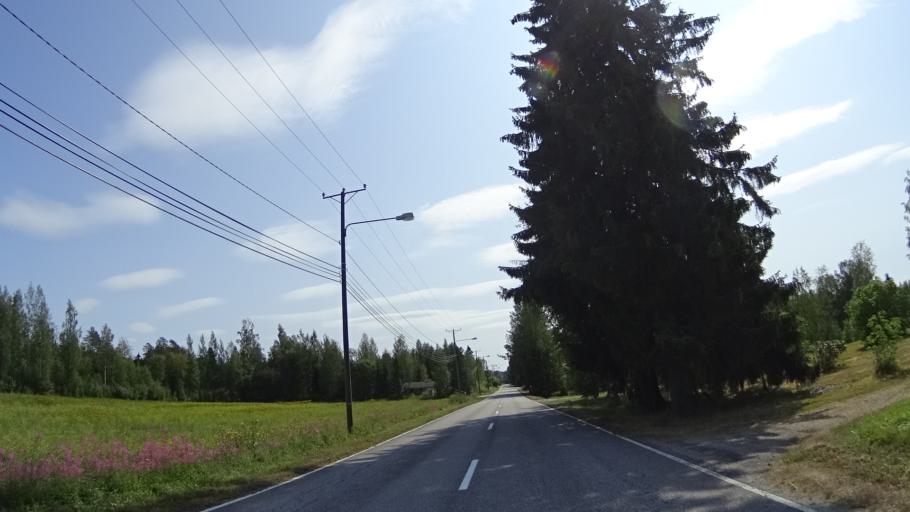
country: FI
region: Pirkanmaa
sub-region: Ylae-Pirkanmaa
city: Maenttae
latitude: 61.9149
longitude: 24.7758
